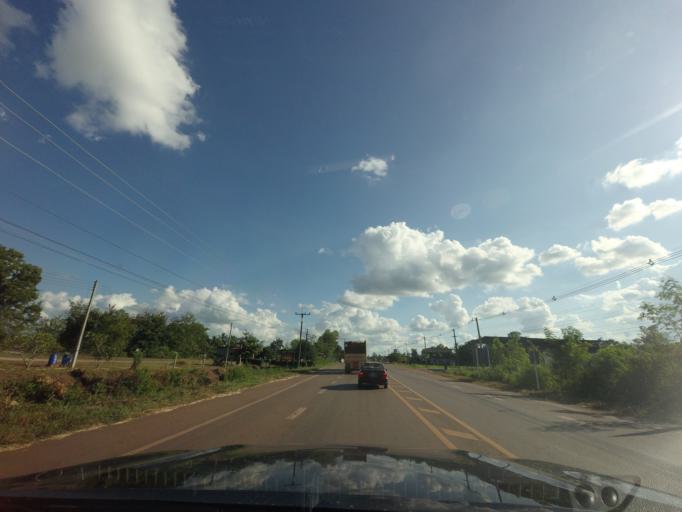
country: TH
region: Changwat Udon Thani
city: Ban Dung
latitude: 17.7300
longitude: 103.2521
